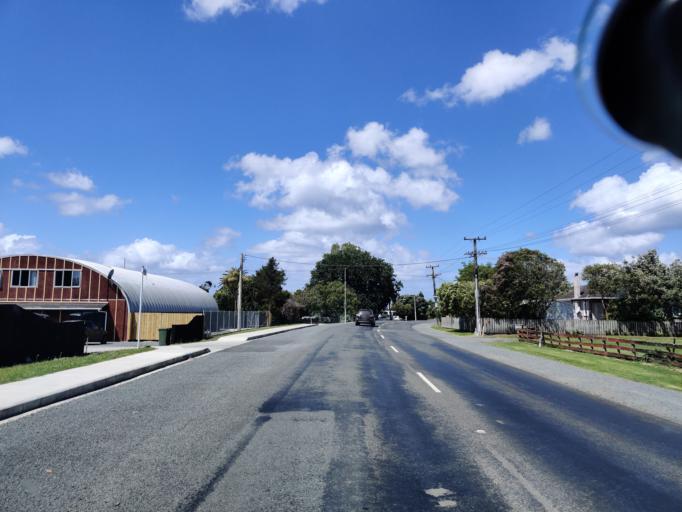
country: NZ
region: Northland
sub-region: Whangarei
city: Ruakaka
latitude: -35.9828
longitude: 174.4371
